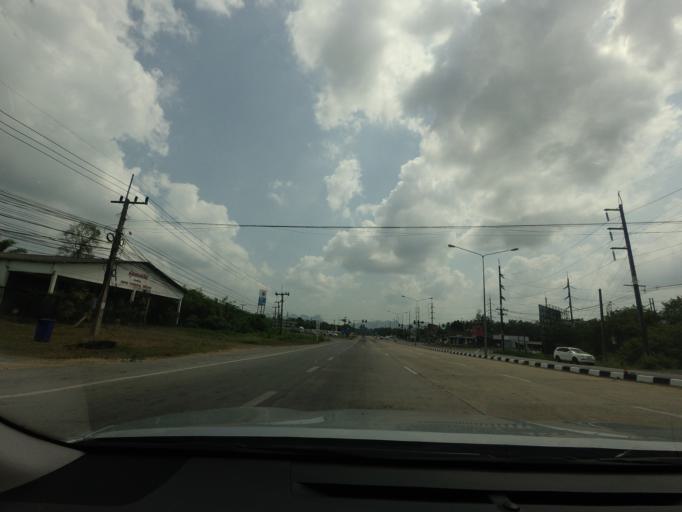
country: TH
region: Phangnga
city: Thap Put
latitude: 8.5071
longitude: 98.6805
